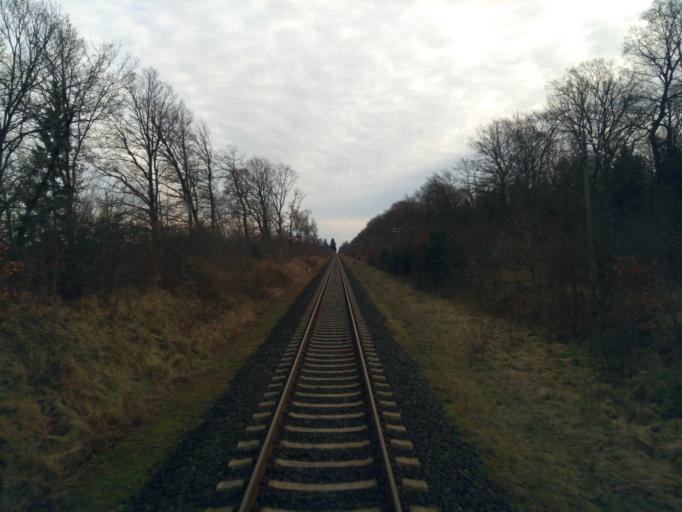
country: DE
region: Lower Saxony
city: Wriedel
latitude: 53.0002
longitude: 10.2367
